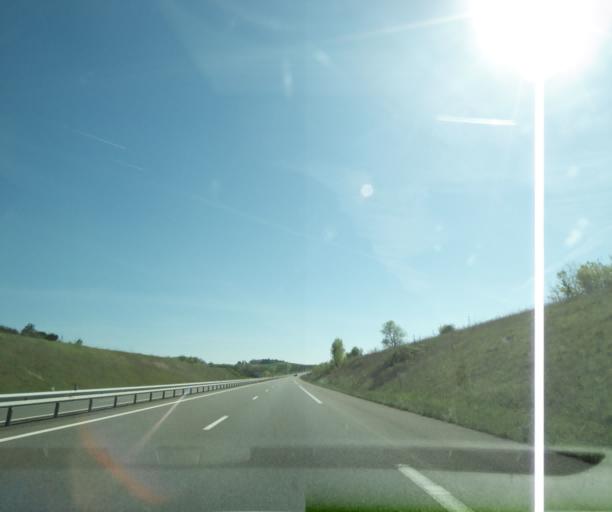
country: FR
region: Midi-Pyrenees
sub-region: Departement du Lot
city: Lalbenque
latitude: 44.2977
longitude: 1.5091
